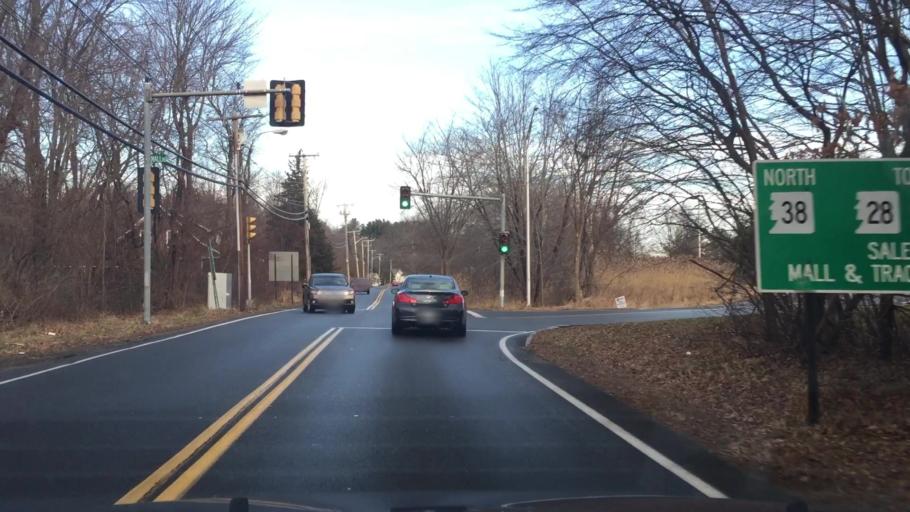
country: US
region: New Hampshire
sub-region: Rockingham County
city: Salem
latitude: 42.7697
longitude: -71.2330
